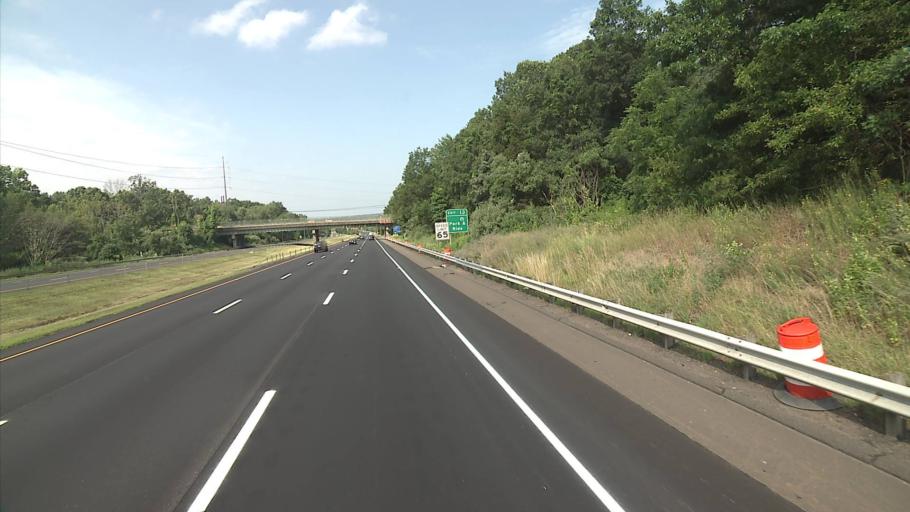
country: US
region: Connecticut
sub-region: New Haven County
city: Wallingford Center
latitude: 41.4292
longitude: -72.8127
